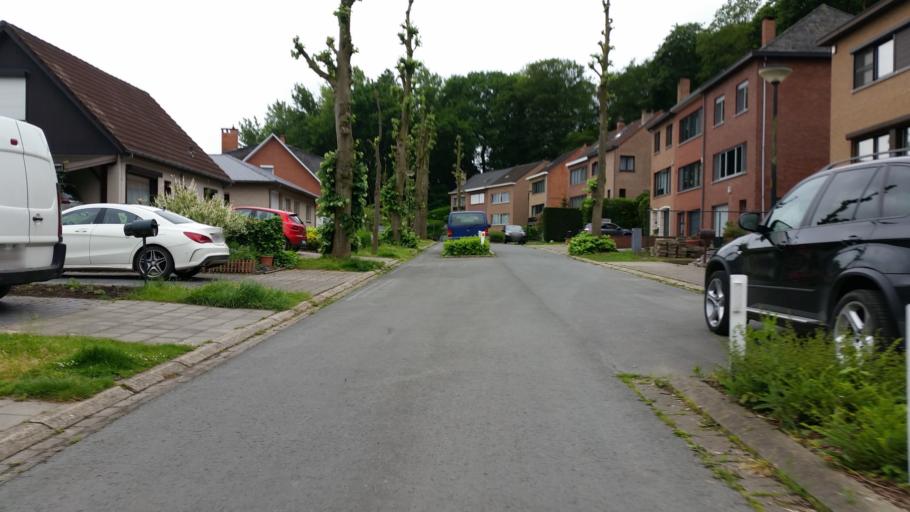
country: BE
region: Flanders
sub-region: Provincie Vlaams-Brabant
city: Vilvoorde
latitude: 50.9172
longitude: 4.4156
